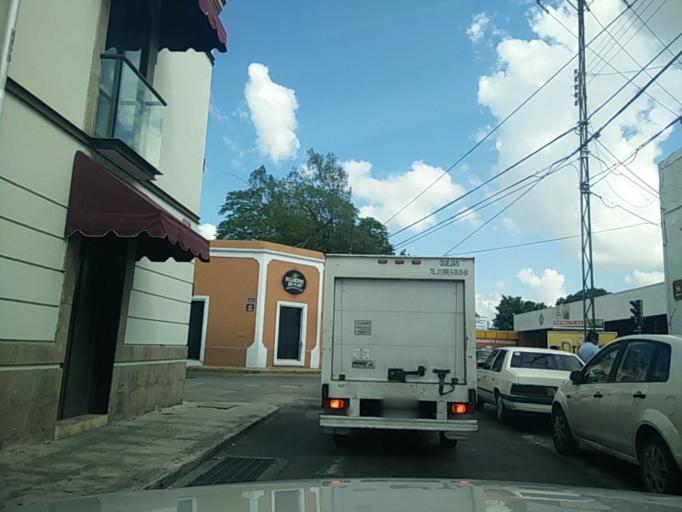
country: MX
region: Yucatan
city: Merida
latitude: 20.9749
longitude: -89.6190
